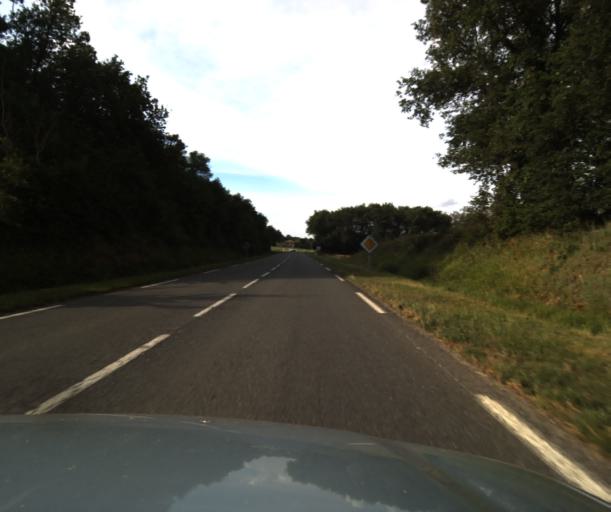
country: FR
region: Midi-Pyrenees
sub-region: Departement du Tarn-et-Garonne
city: Beaumont-de-Lomagne
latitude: 43.7768
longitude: 0.8866
